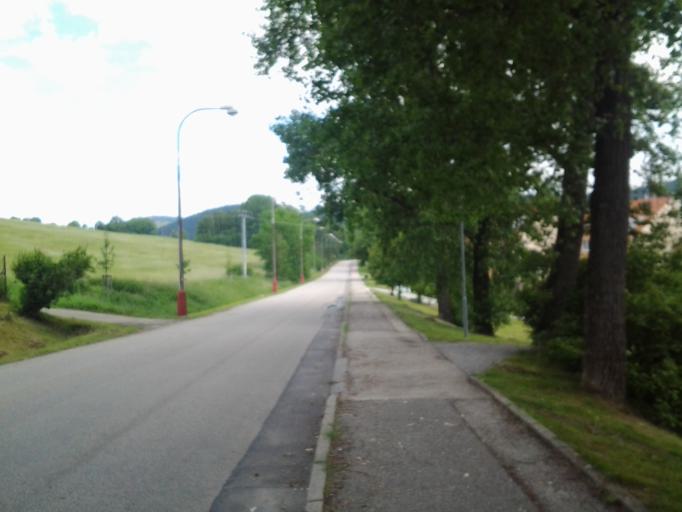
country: CZ
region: Jihocesky
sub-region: Okres Cesky Krumlov
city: Cesky Krumlov
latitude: 48.8231
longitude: 14.3098
